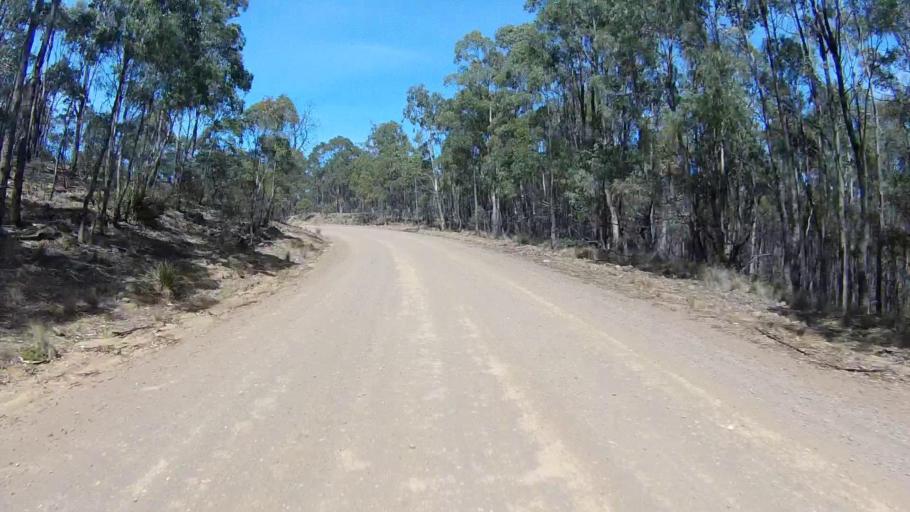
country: AU
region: Tasmania
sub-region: Sorell
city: Sorell
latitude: -42.6722
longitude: 147.7263
